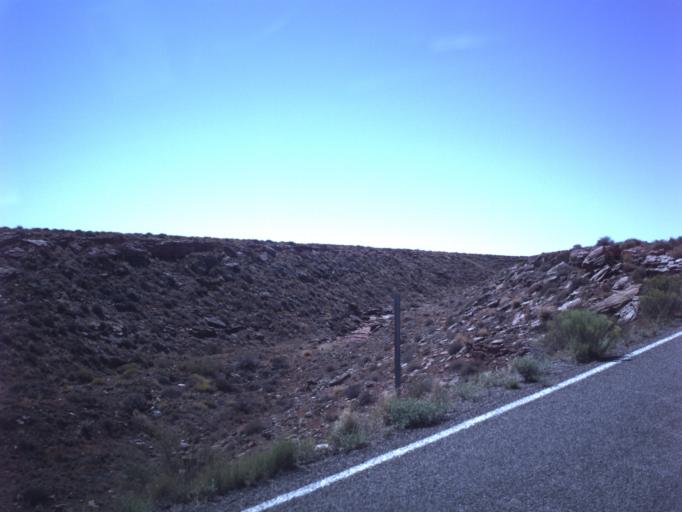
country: US
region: Utah
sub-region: San Juan County
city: Blanding
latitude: 37.2000
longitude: -109.8838
